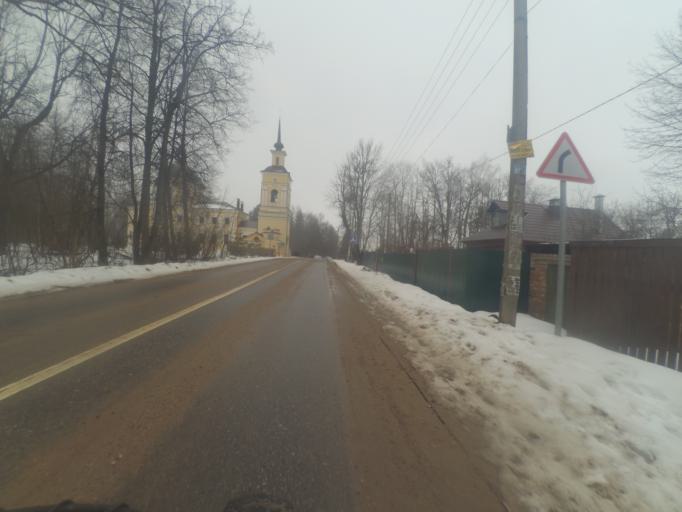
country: RU
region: Moskovskaya
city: Avtopoligon
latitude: 56.2592
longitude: 37.2474
